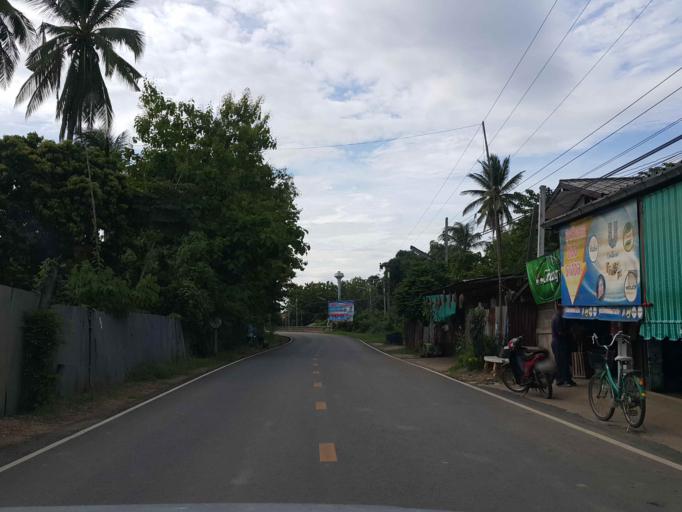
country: TH
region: Sukhothai
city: Thung Saliam
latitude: 17.3241
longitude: 99.5172
